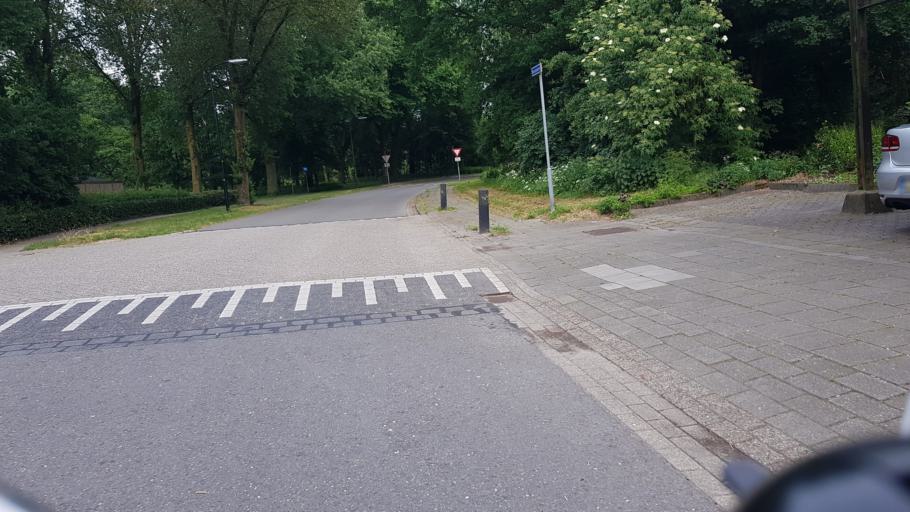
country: NL
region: Gelderland
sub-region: Gemeente Apeldoorn
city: Apeldoorn
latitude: 52.1971
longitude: 6.0163
